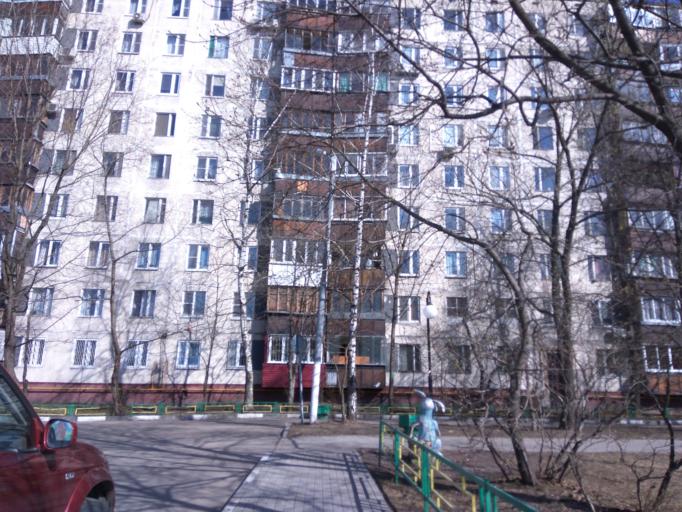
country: RU
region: Moscow
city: Ivanovskoye
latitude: 55.7720
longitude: 37.8385
